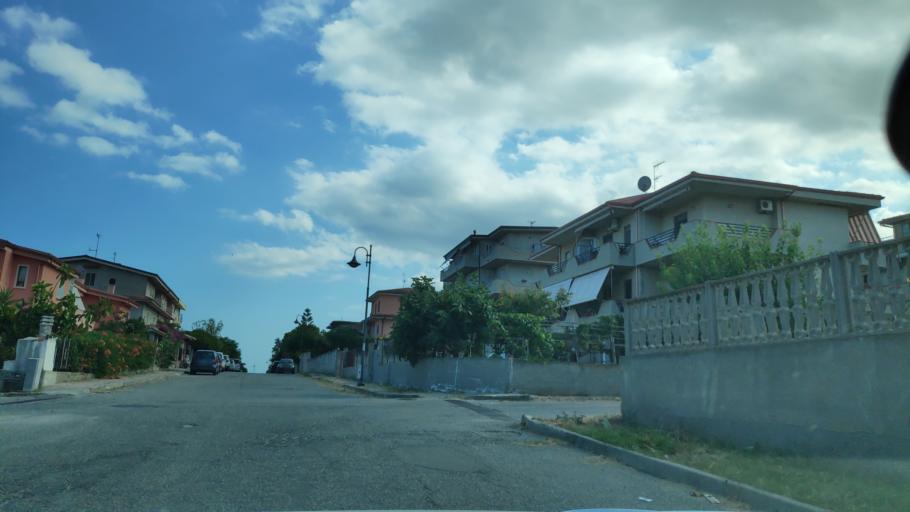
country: IT
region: Calabria
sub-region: Provincia di Catanzaro
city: Guardavalle Marina
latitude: 38.4729
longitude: 16.5779
